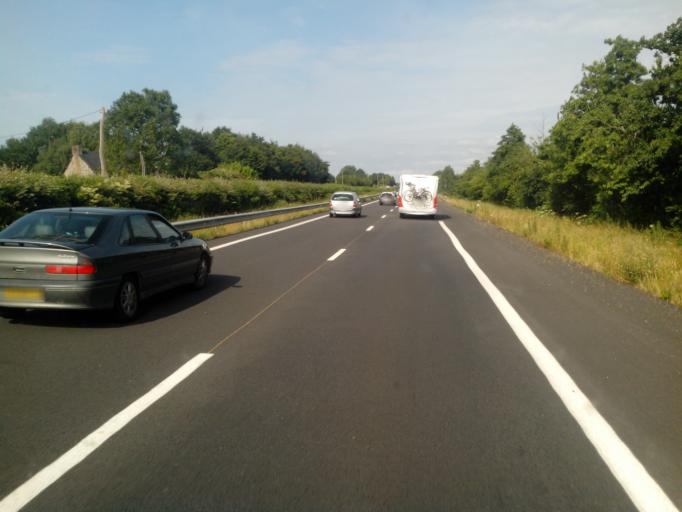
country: FR
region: Brittany
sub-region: Departement d'Ille-et-Vilaine
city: Monterfil
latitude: 48.0321
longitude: -1.9921
